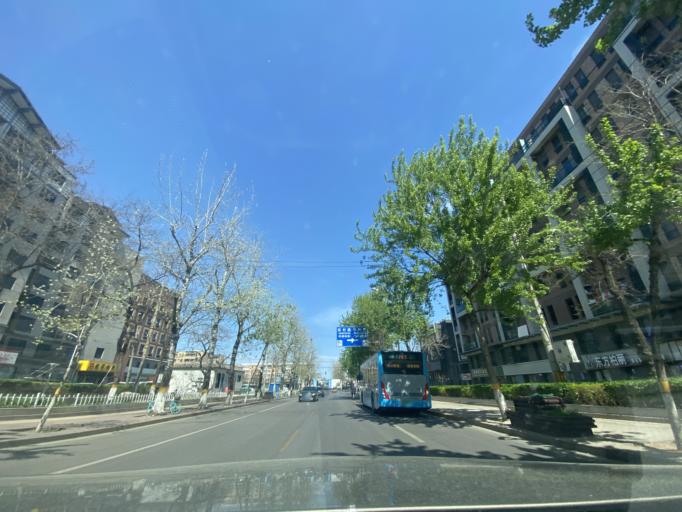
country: CN
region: Beijing
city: Sijiqing
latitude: 39.9265
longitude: 116.2587
